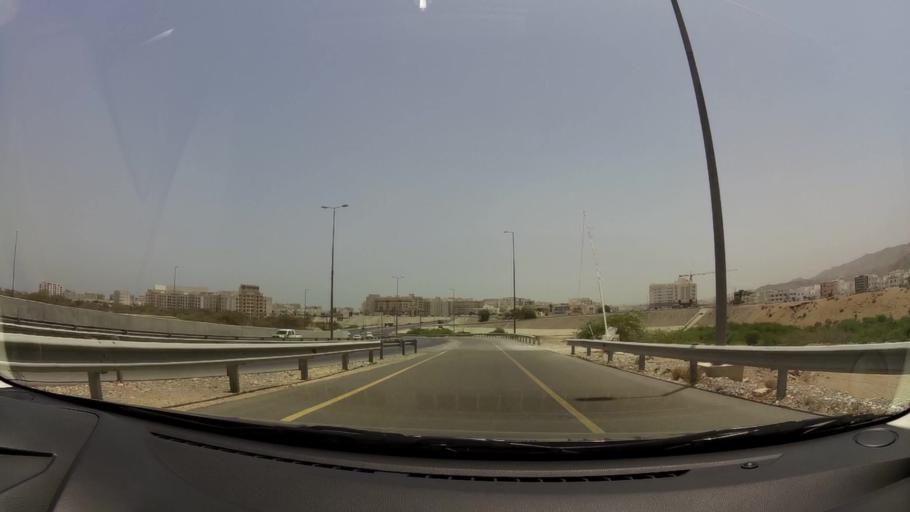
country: OM
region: Muhafazat Masqat
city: Bawshar
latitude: 23.5817
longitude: 58.4186
